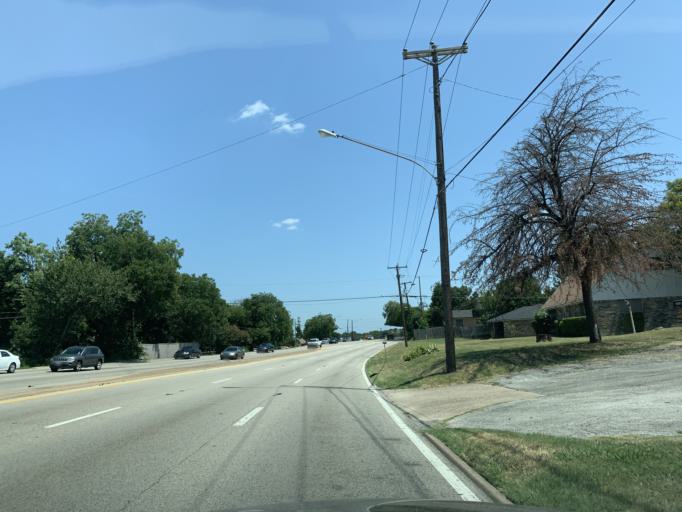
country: US
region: Texas
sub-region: Dallas County
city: Cockrell Hill
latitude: 32.6835
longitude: -96.8099
